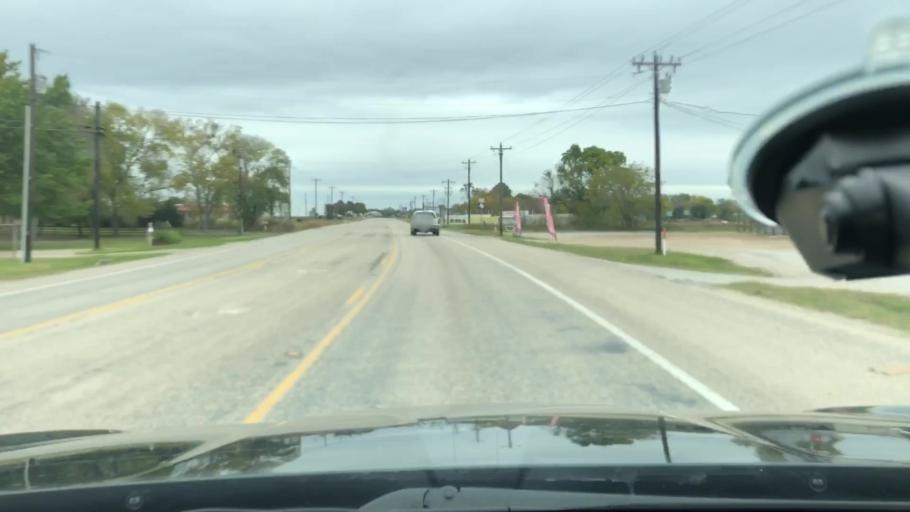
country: US
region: Texas
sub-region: Hunt County
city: Greenville
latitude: 33.0361
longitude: -96.1069
